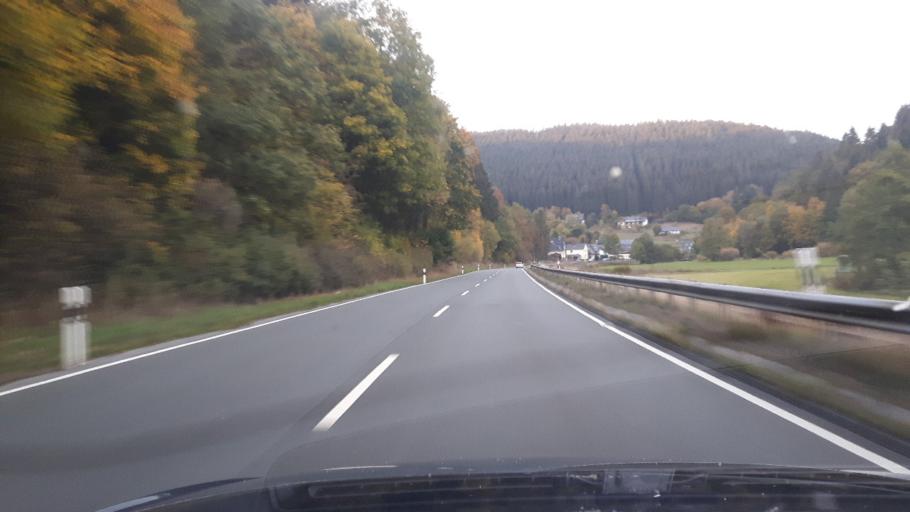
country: DE
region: North Rhine-Westphalia
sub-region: Regierungsbezirk Arnsberg
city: Erndtebruck
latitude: 50.9468
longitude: 8.3405
